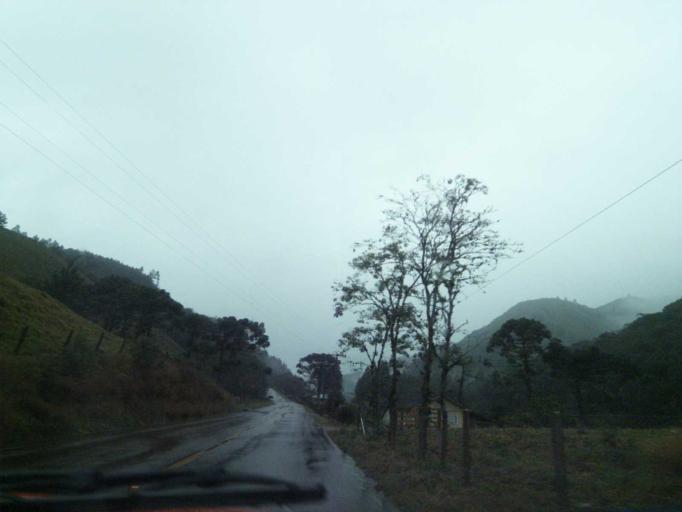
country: BR
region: Santa Catarina
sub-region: Anitapolis
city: Anitapolis
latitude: -27.8262
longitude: -49.0504
